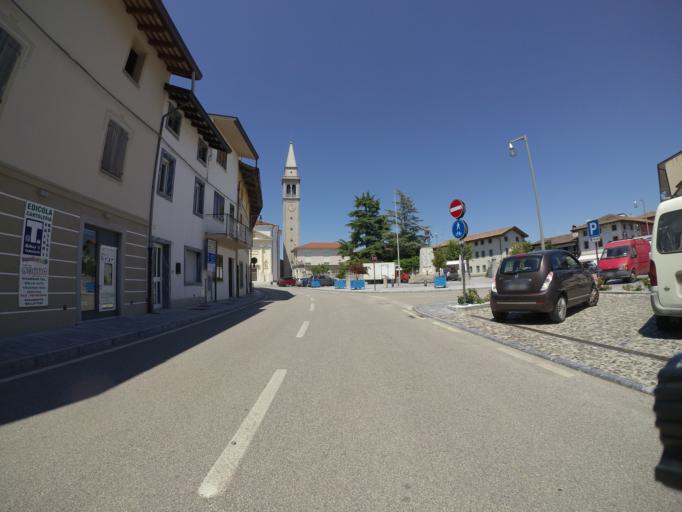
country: IT
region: Friuli Venezia Giulia
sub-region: Provincia di Udine
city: Talmassons
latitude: 45.9283
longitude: 13.1170
